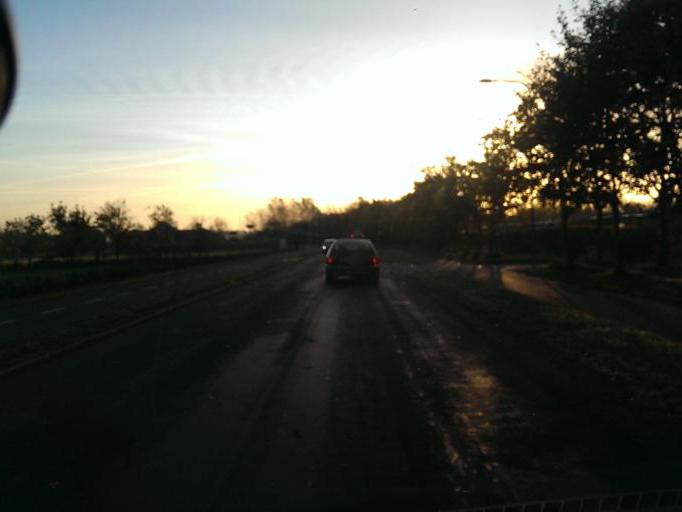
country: DK
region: South Denmark
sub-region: Esbjerg Kommune
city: Tjaereborg
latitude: 55.4599
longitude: 8.5951
